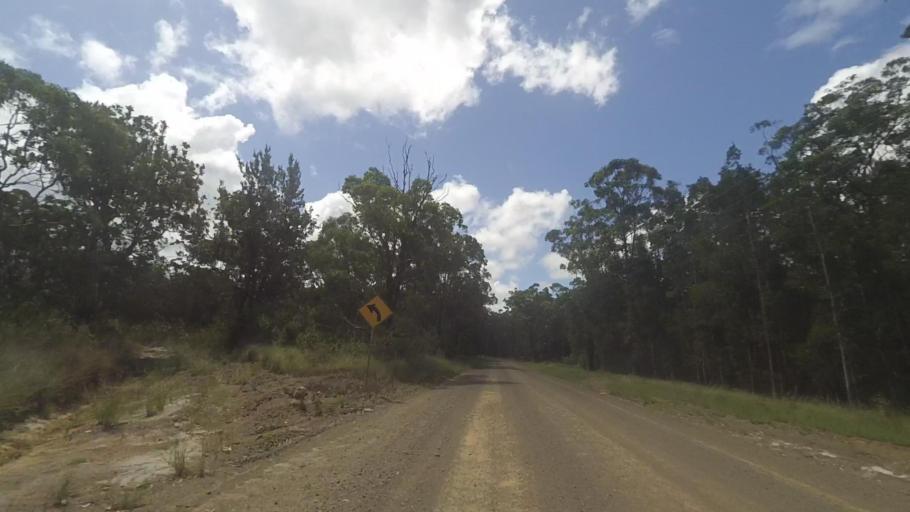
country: AU
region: New South Wales
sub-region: Great Lakes
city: Bulahdelah
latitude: -32.5041
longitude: 152.2907
